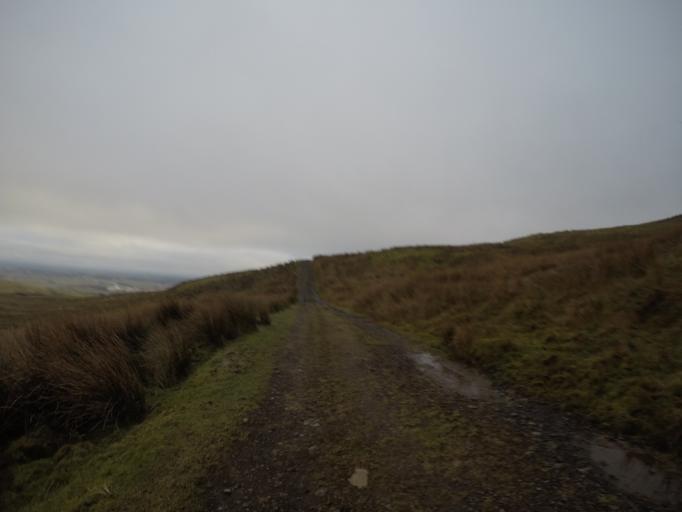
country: GB
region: Scotland
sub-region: North Ayrshire
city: Dalry
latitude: 55.7350
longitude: -4.7687
